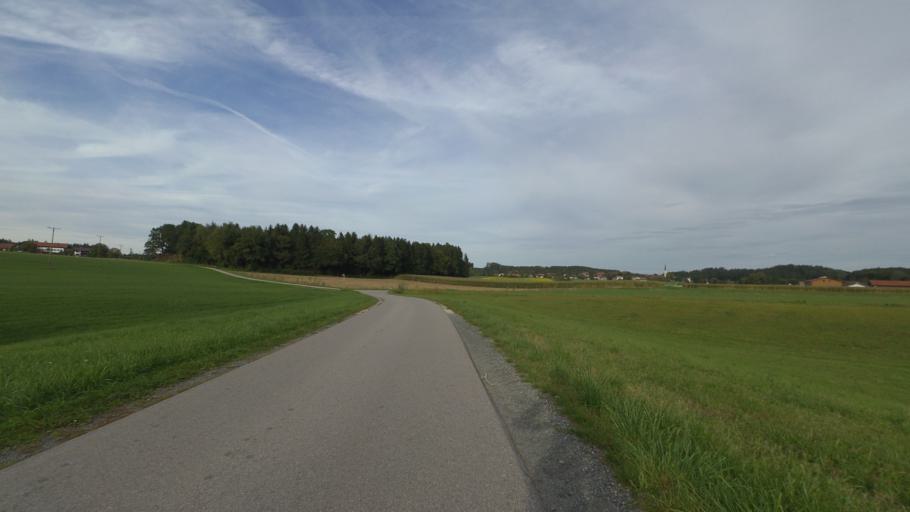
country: DE
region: Bavaria
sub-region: Upper Bavaria
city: Chieming
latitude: 47.9243
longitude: 12.5346
